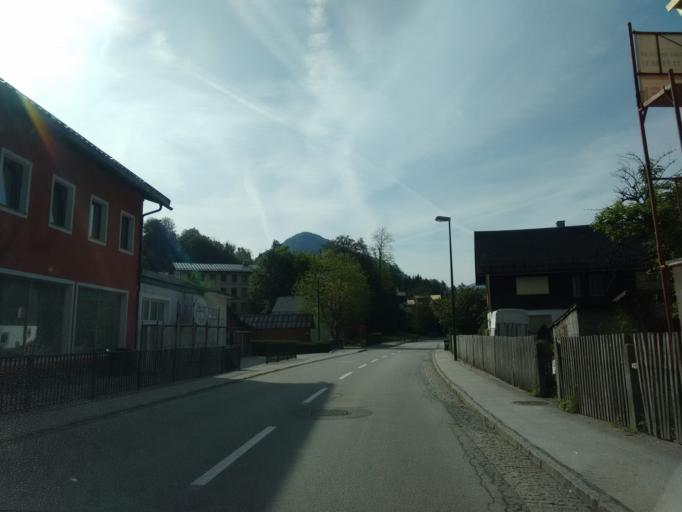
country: AT
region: Styria
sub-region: Politischer Bezirk Liezen
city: Bad Aussee
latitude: 47.6186
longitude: 13.7734
